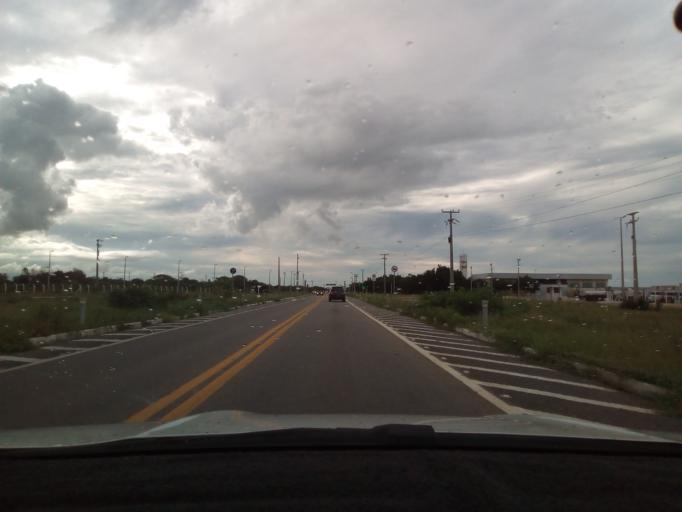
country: BR
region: Ceara
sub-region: Aracati
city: Aracati
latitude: -4.6216
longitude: -37.6490
